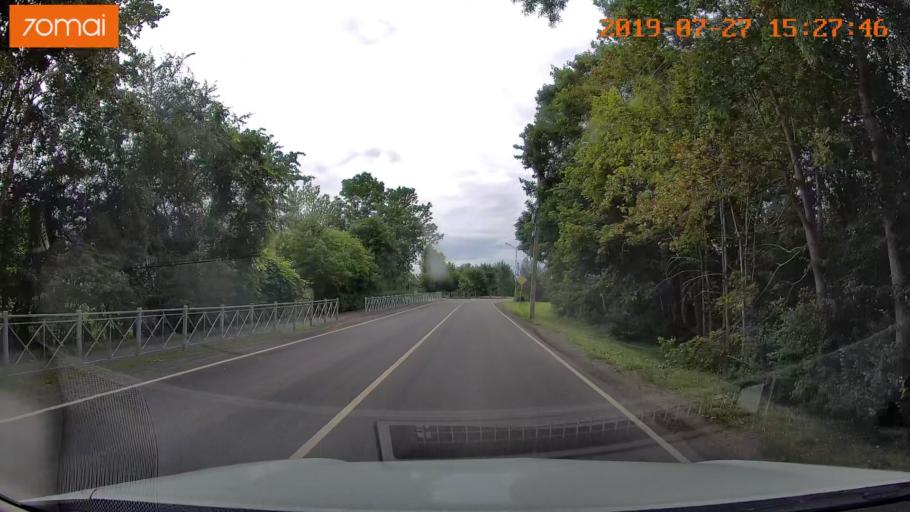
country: RU
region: Kaliningrad
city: Nesterov
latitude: 54.6336
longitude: 22.5593
